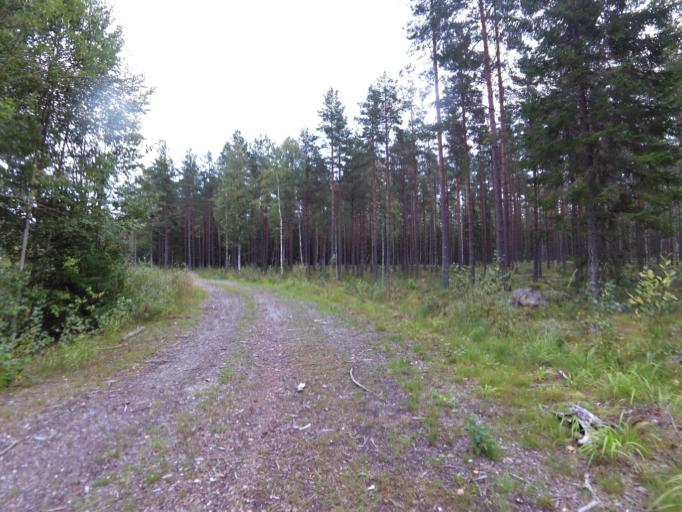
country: SE
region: Gaevleborg
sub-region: Gavle Kommun
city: Valbo
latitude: 60.7238
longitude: 17.0291
